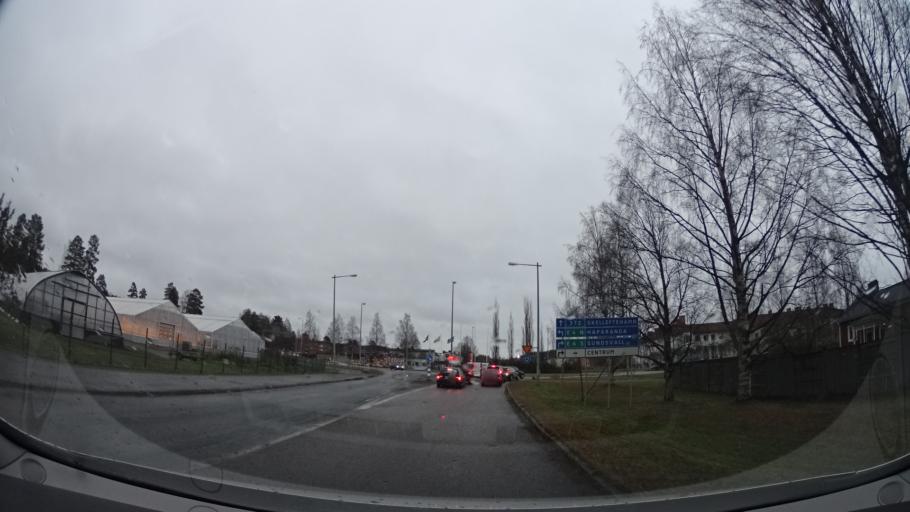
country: SE
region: Vaesterbotten
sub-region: Skelleftea Kommun
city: Skelleftea
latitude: 64.7580
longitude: 20.9630
